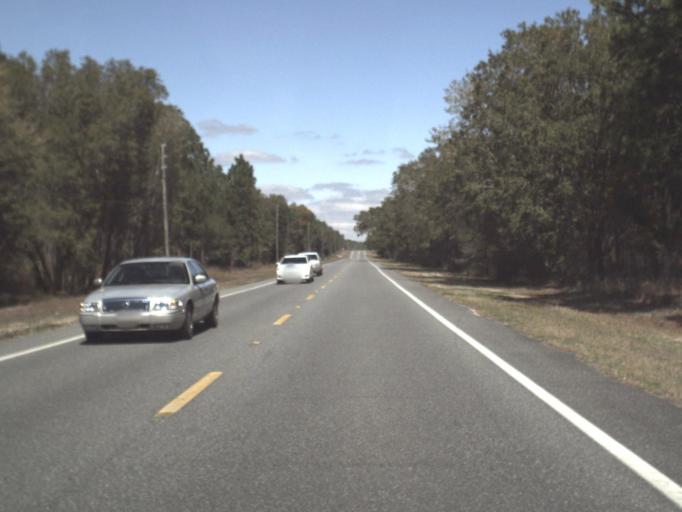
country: US
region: Florida
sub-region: Wakulla County
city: Crawfordville
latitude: 30.0594
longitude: -84.3884
